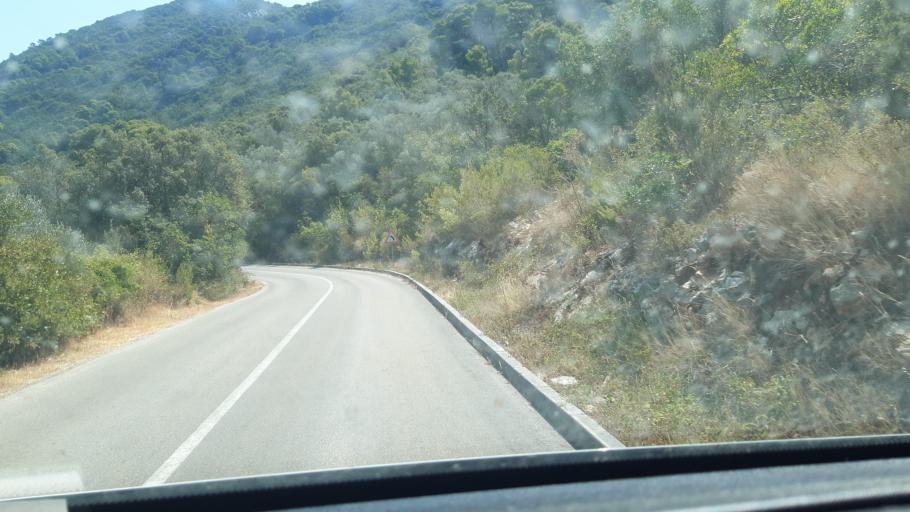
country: HR
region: Dubrovacko-Neretvanska
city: Ston
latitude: 42.7231
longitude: 17.6675
